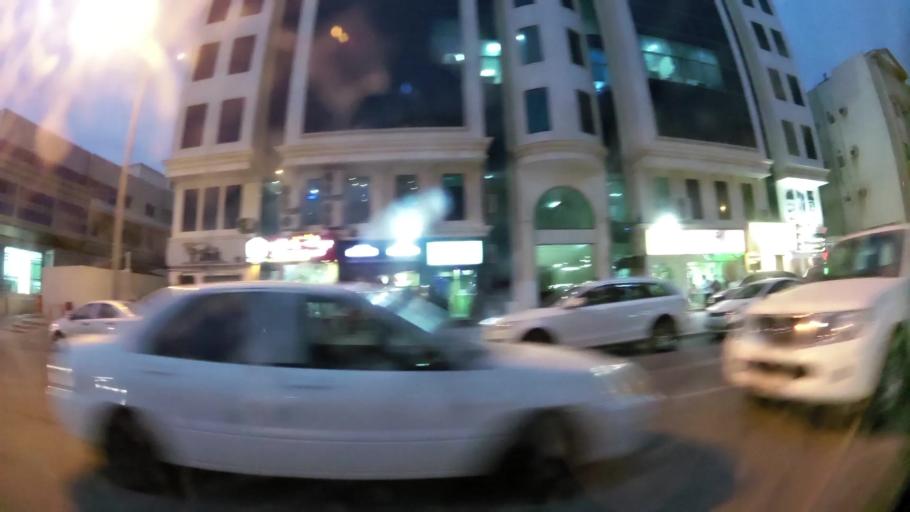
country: QA
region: Baladiyat ad Dawhah
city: Doha
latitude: 25.2672
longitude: 51.5195
